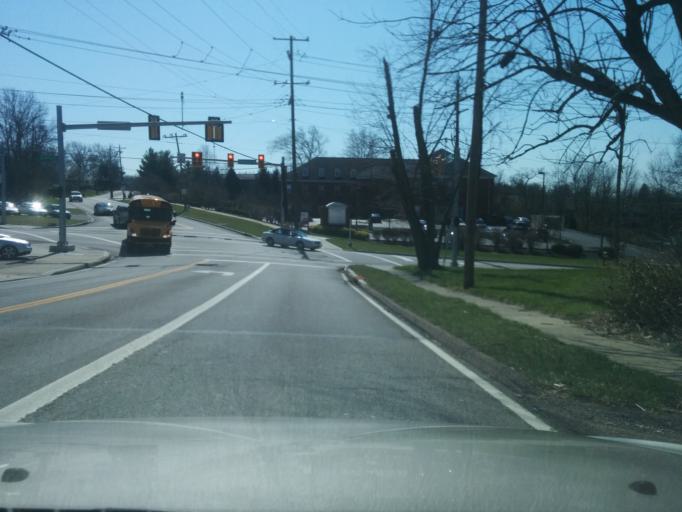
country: US
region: Ohio
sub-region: Hamilton County
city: White Oak
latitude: 39.2212
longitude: -84.6015
